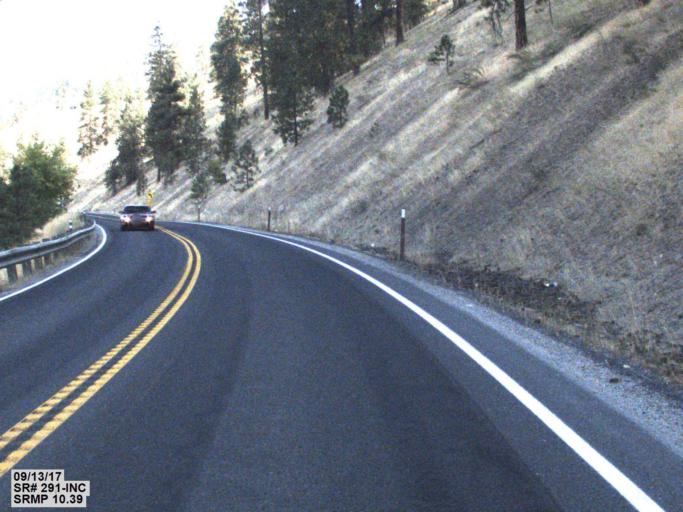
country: US
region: Washington
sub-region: Spokane County
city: Fairwood
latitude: 47.7873
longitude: -117.5272
